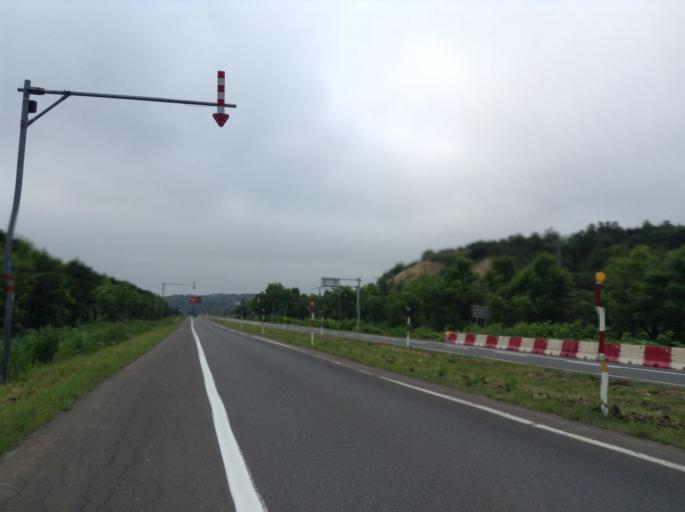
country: JP
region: Hokkaido
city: Wakkanai
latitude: 45.3673
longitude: 141.7279
